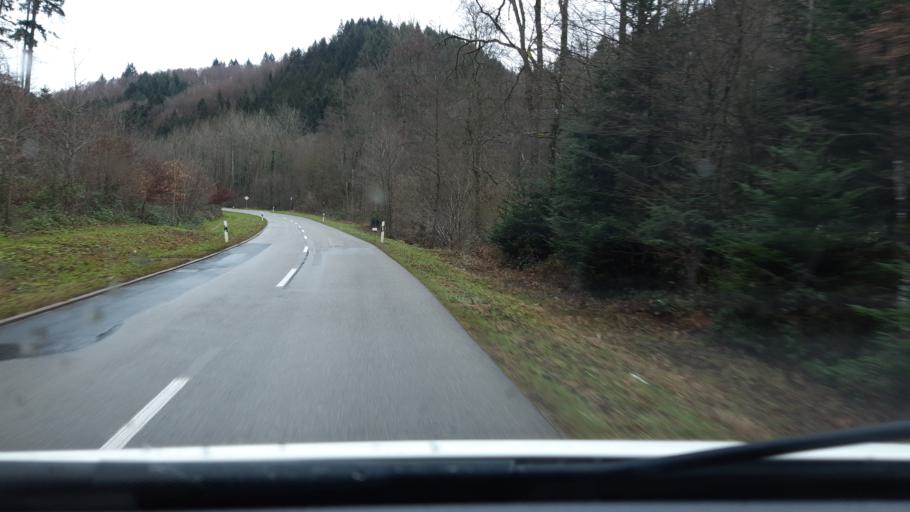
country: DE
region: Baden-Wuerttemberg
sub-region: Freiburg Region
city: Solden
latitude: 47.9154
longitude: 7.8113
